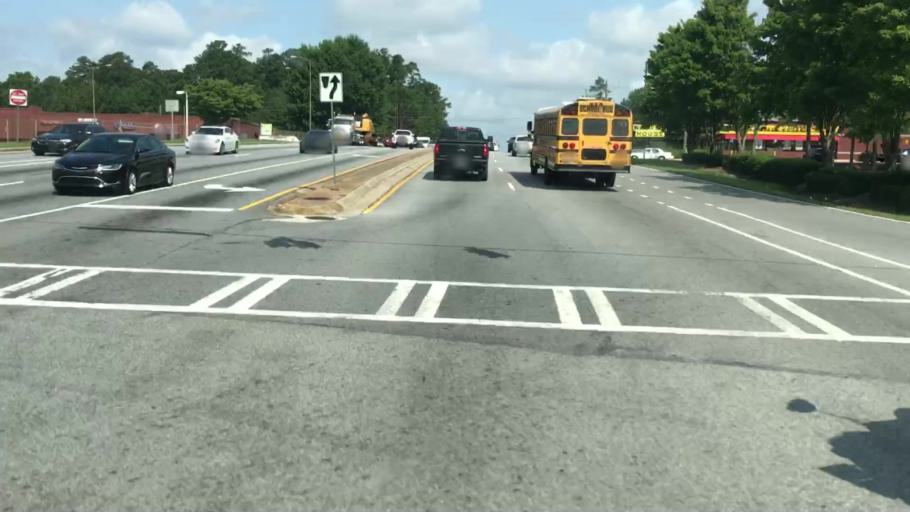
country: US
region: Georgia
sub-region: Gwinnett County
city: Lawrenceville
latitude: 33.9385
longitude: -84.0339
